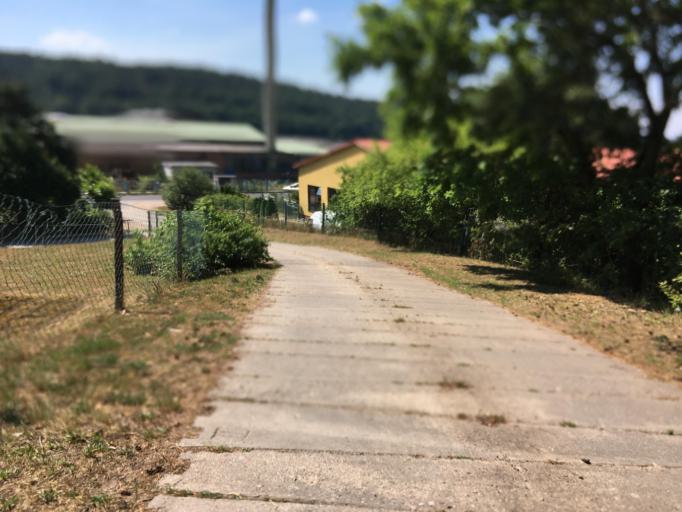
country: DE
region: Brandenburg
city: Joachimsthal
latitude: 52.9566
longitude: 13.7366
